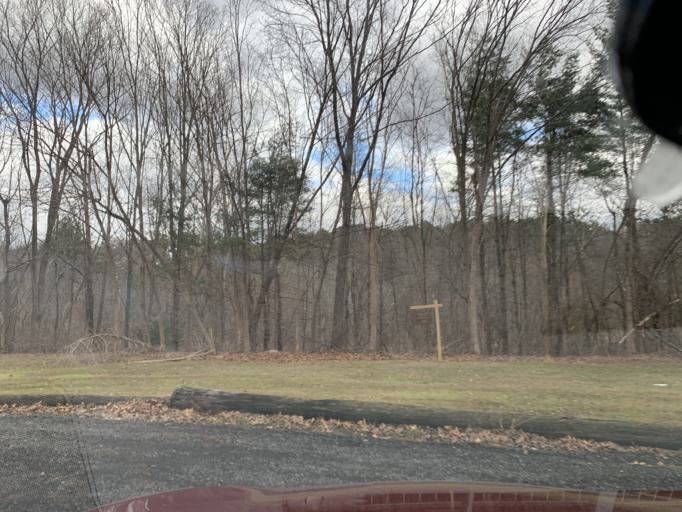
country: US
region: Massachusetts
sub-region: Essex County
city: Merrimac
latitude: 42.8284
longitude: -70.9891
